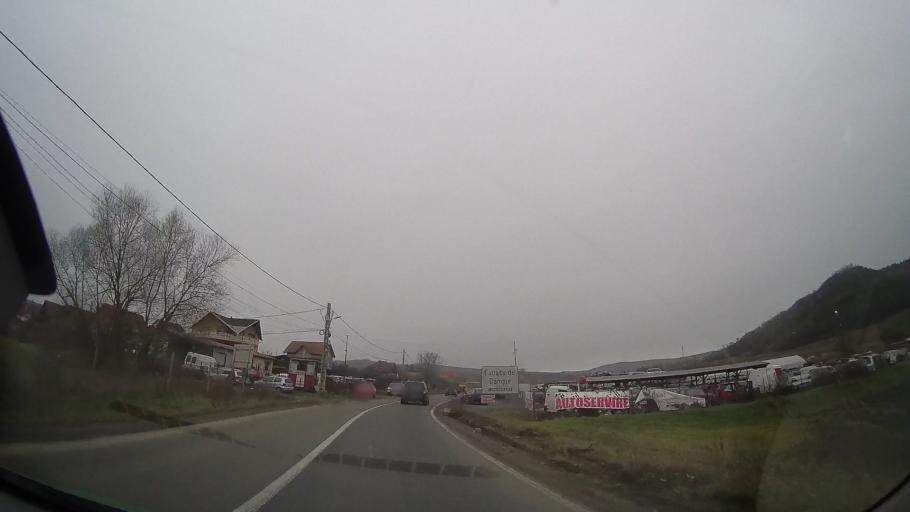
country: RO
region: Mures
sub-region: Comuna Ceausu de Campie
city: Ceausu de Campie
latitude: 46.6317
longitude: 24.5189
